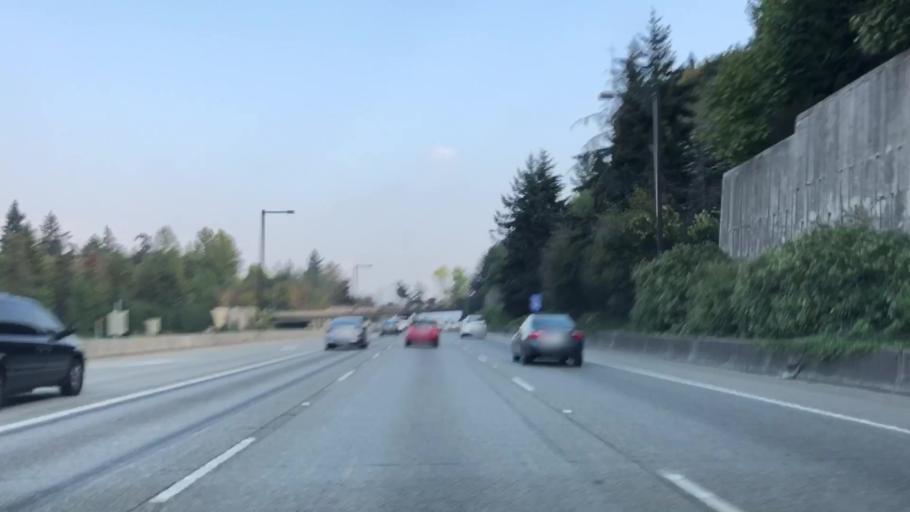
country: US
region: Washington
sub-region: King County
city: Mercer Island
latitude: 47.5819
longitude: -122.2213
